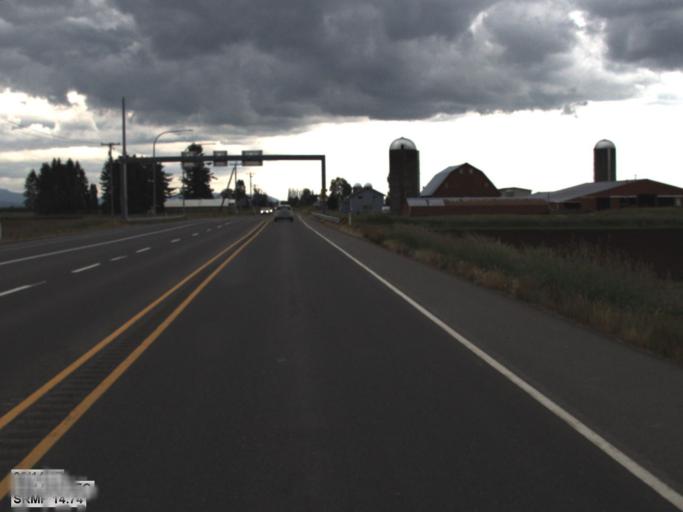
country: US
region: Washington
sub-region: Whatcom County
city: Lynden
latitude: 48.9961
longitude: -122.4851
